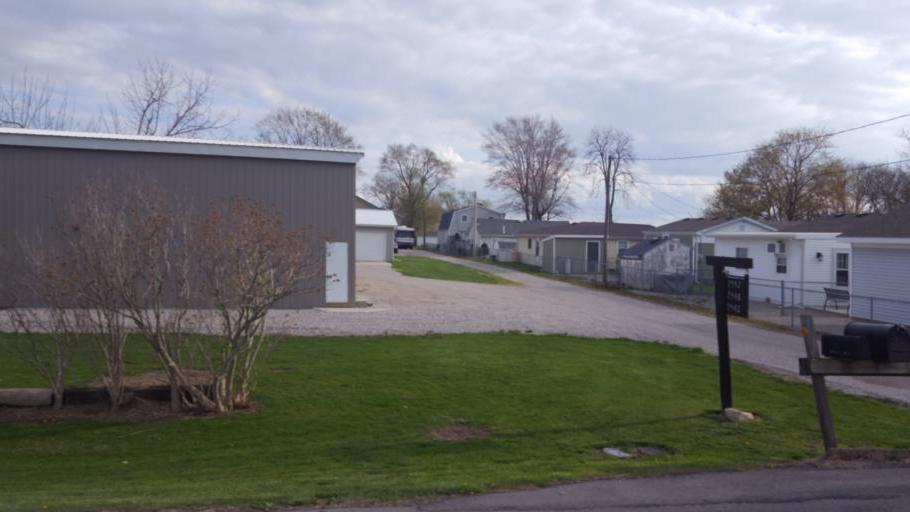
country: US
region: Ohio
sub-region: Erie County
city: Sandusky
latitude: 41.5084
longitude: -82.7893
